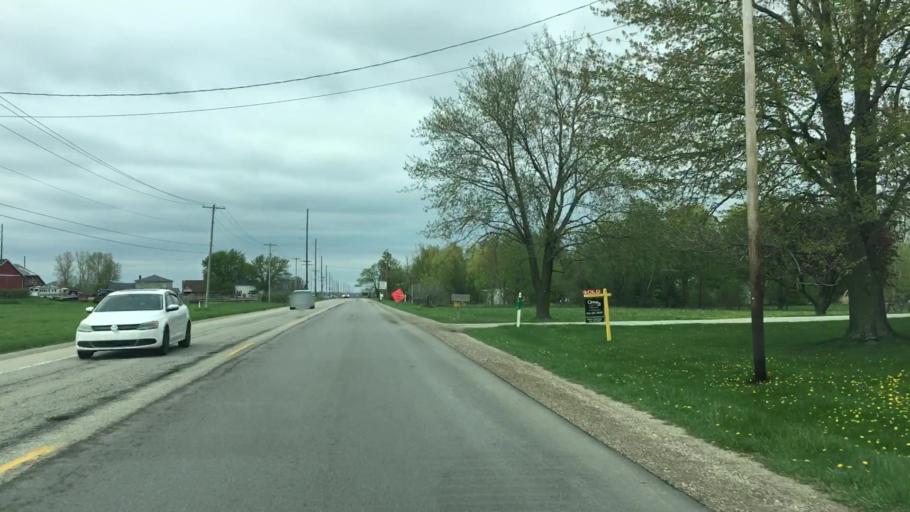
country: US
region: Michigan
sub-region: Ottawa County
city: Hudsonville
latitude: 42.8303
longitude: -85.8619
